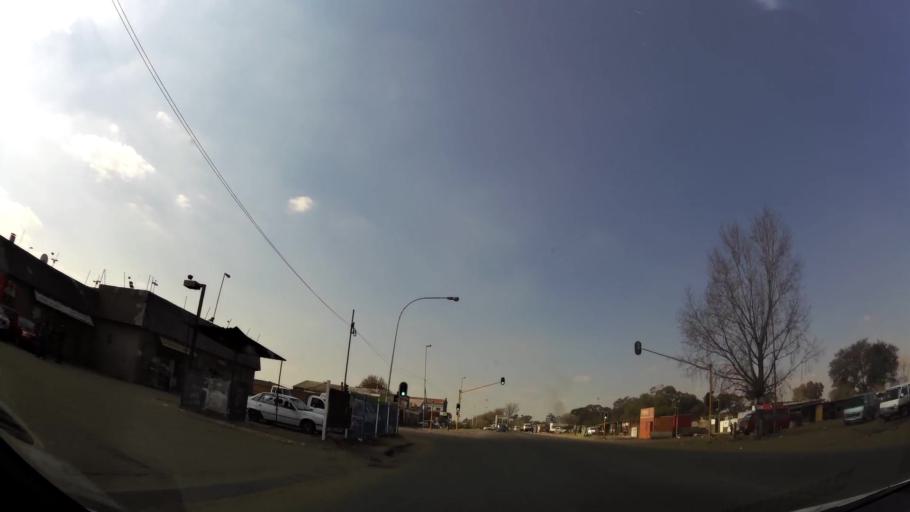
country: ZA
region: Gauteng
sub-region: Ekurhuleni Metropolitan Municipality
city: Boksburg
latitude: -26.1983
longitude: 28.2156
